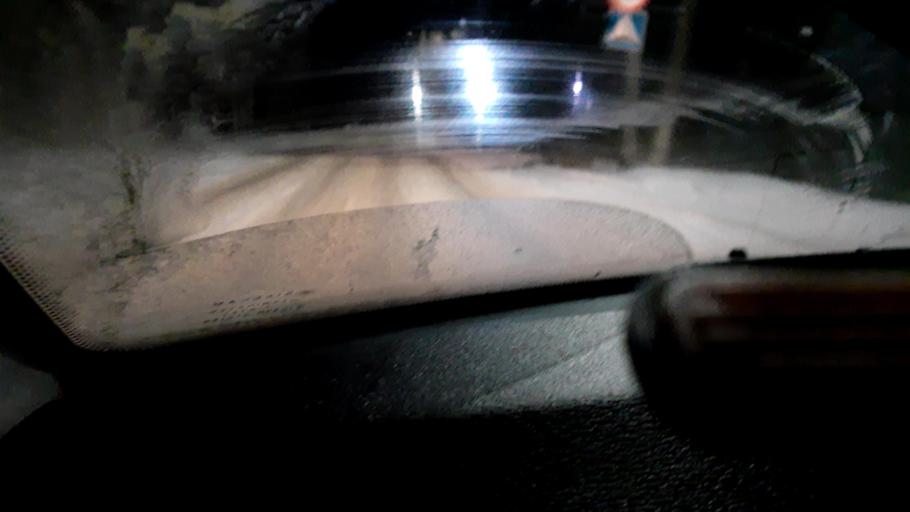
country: RU
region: Nizjnij Novgorod
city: Bogorodsk
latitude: 56.1049
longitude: 43.4802
